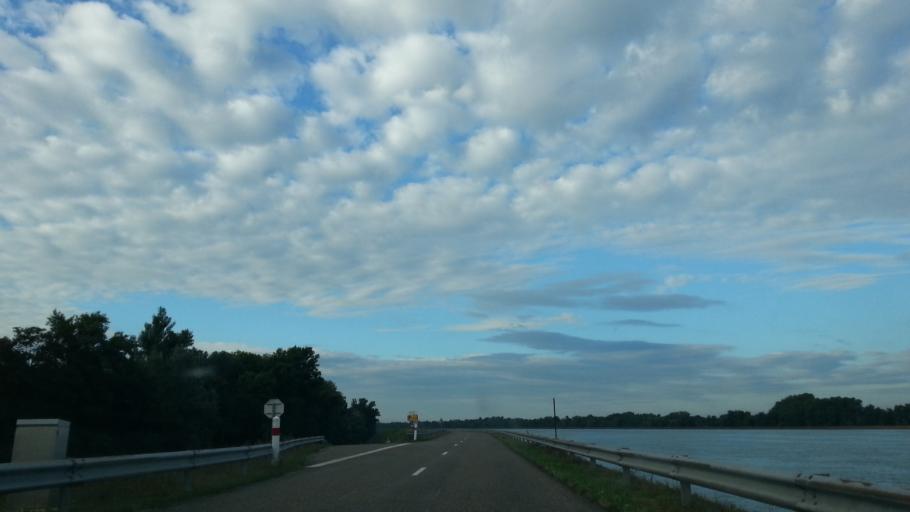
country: FR
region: Alsace
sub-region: Departement du Bas-Rhin
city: Gerstheim
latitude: 48.3915
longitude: 7.7254
